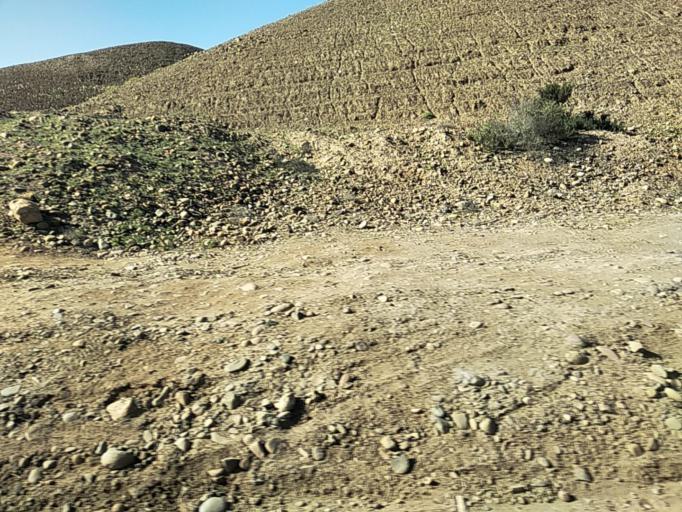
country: CL
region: Atacama
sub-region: Provincia de Copiapo
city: Copiapo
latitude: -27.3379
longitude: -70.7685
